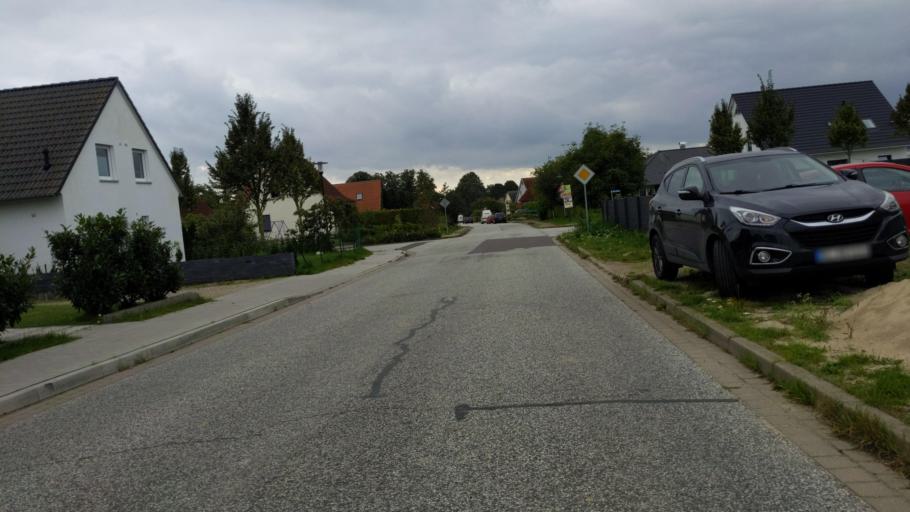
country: DE
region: Schleswig-Holstein
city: Gross Gronau
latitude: 53.7704
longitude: 10.7742
